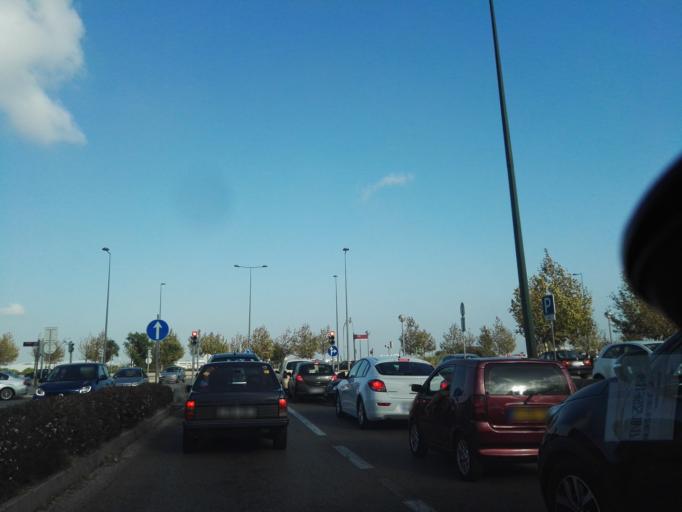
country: PT
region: Lisbon
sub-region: Odivelas
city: Olival do Basto
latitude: 38.7673
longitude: -9.1493
